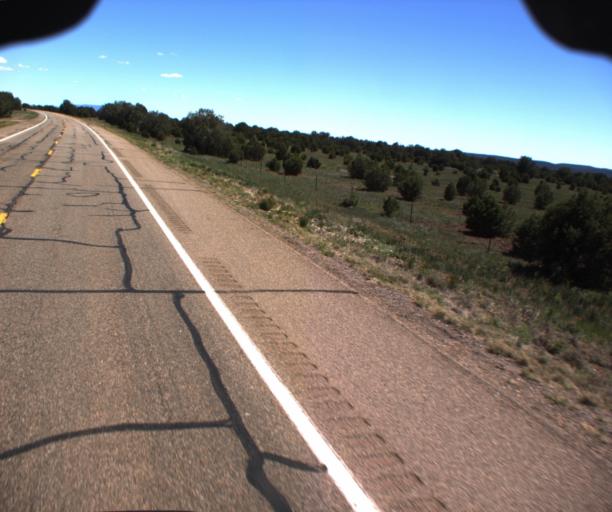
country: US
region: Arizona
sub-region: Yavapai County
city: Paulden
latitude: 35.0986
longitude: -112.4230
